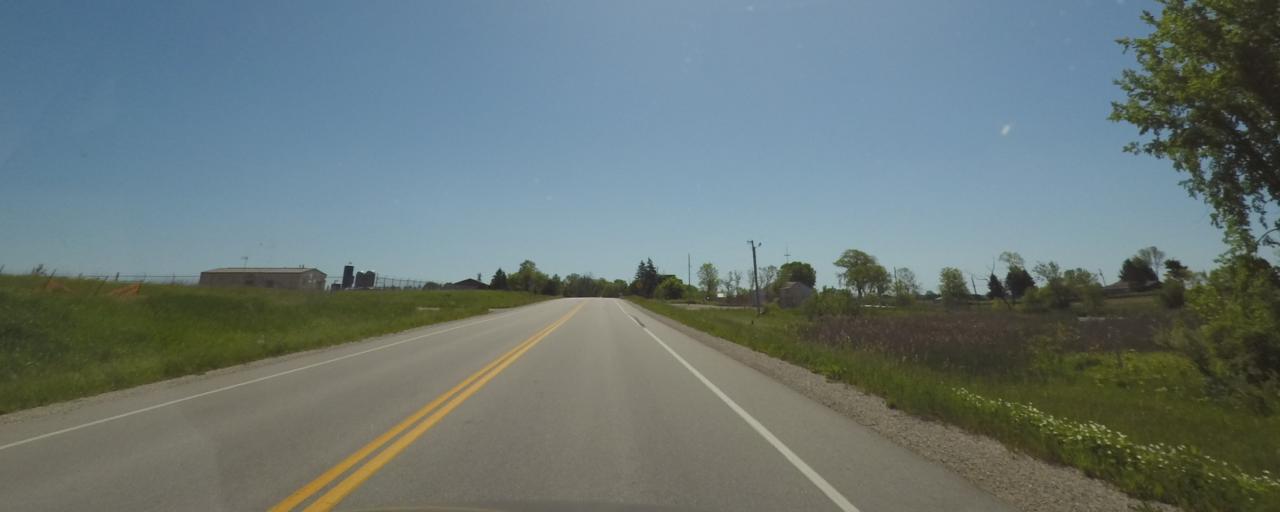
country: US
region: Wisconsin
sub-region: Sheboygan County
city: Sheboygan Falls
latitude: 43.7479
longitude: -87.8955
